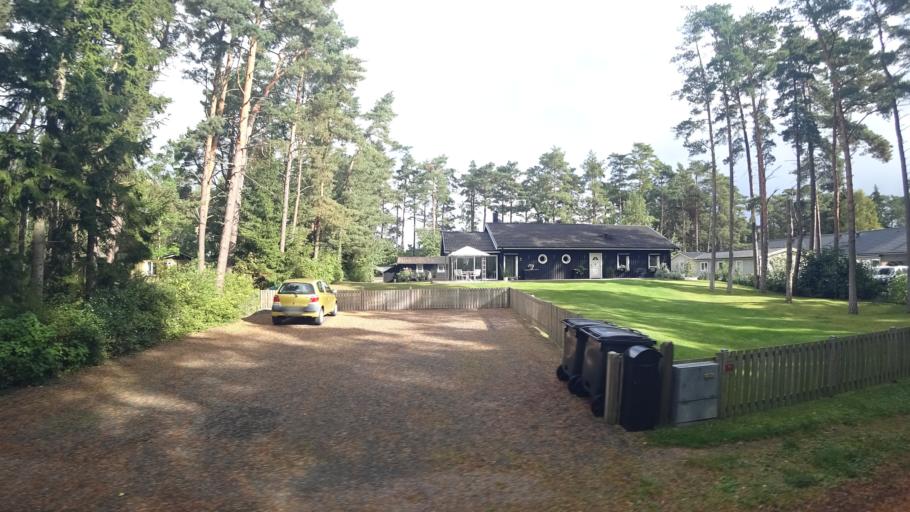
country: SE
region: Skane
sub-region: Kristianstads Kommun
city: Ahus
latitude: 55.9391
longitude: 14.3046
